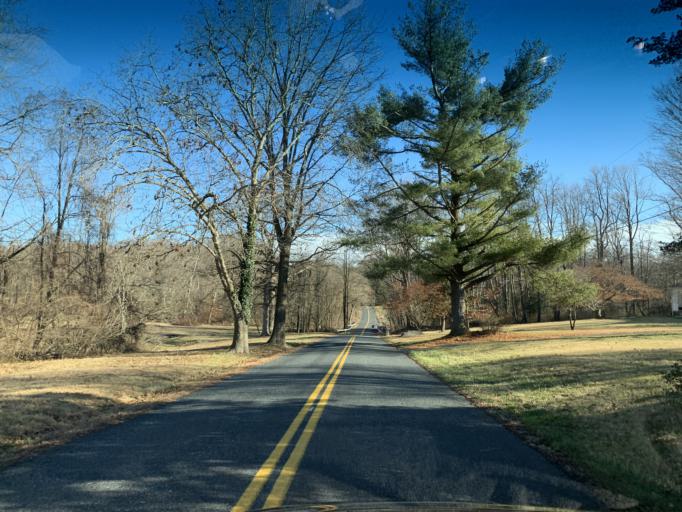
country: US
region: Maryland
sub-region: Harford County
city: Riverside
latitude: 39.5445
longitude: -76.2493
